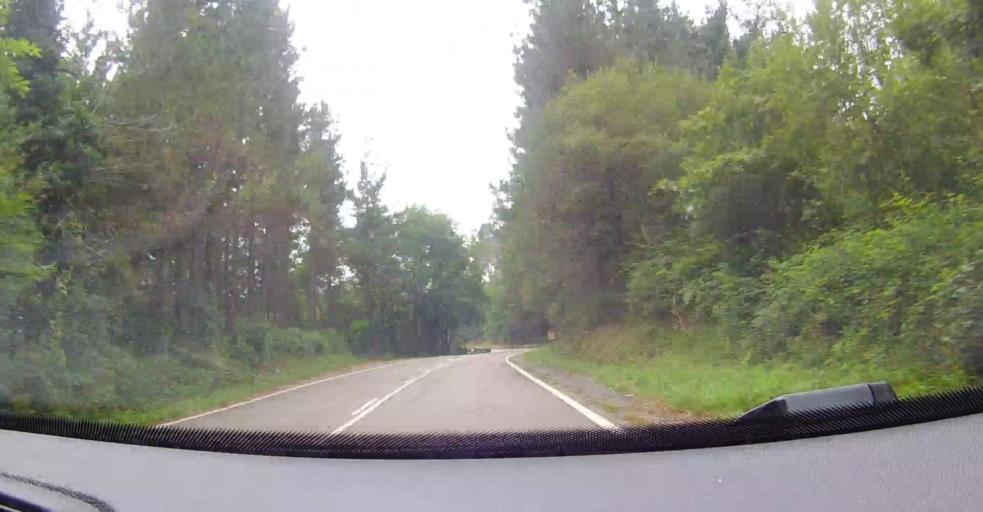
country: ES
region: Basque Country
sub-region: Bizkaia
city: Balmaseda
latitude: 43.2450
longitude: -3.2840
